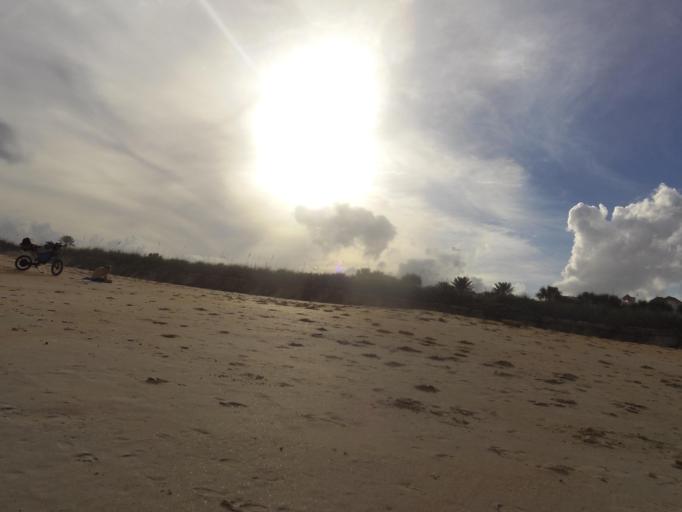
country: US
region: Florida
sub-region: Flagler County
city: Palm Coast
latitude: 29.6056
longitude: -81.1853
